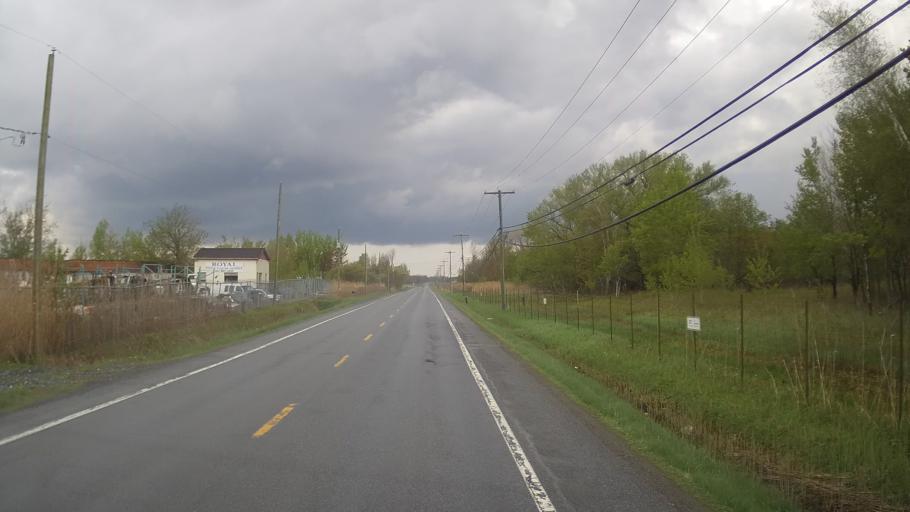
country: CA
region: Quebec
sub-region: Monteregie
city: Farnham
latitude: 45.3081
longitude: -73.0432
